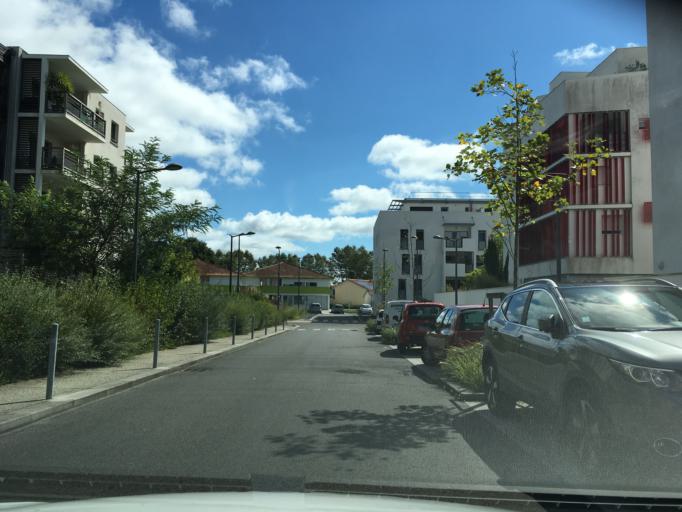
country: FR
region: Aquitaine
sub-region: Departement des Pyrenees-Atlantiques
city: Boucau
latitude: 43.5069
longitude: -1.4594
